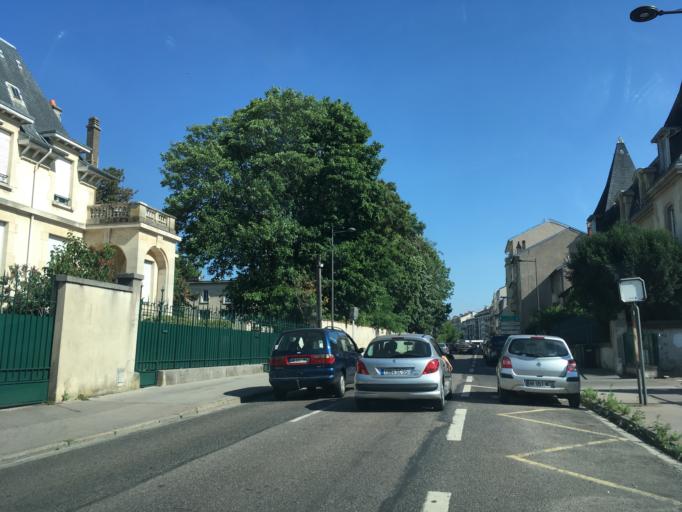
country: FR
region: Lorraine
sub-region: Departement de Meurthe-et-Moselle
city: Nancy
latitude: 48.6792
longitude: 6.1764
